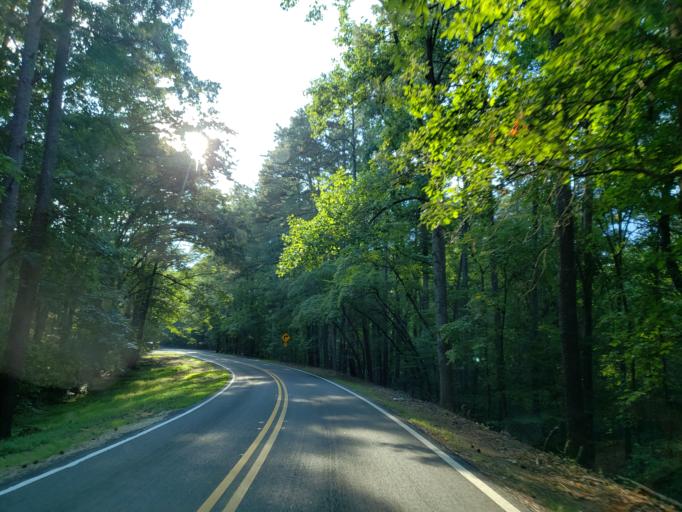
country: US
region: Georgia
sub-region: Bartow County
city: Emerson
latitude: 34.1714
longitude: -84.7330
